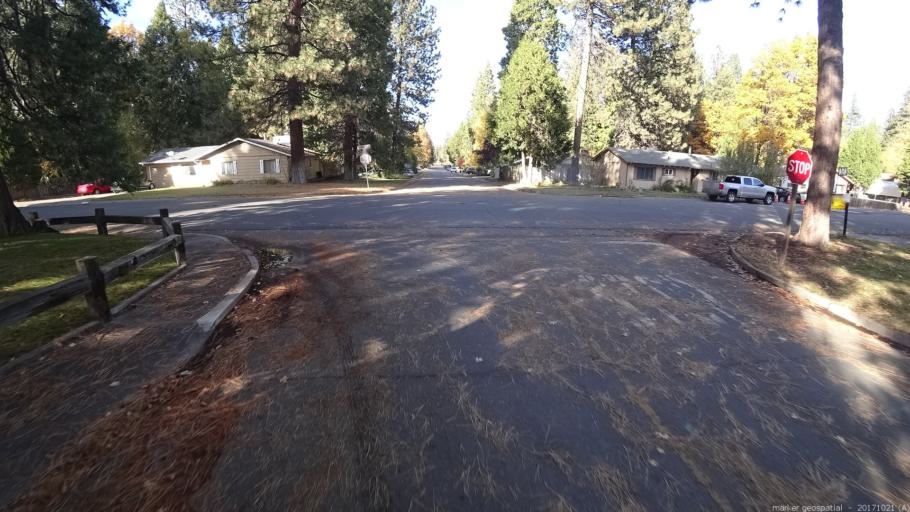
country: US
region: California
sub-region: Shasta County
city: Burney
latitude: 40.8767
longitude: -121.6549
